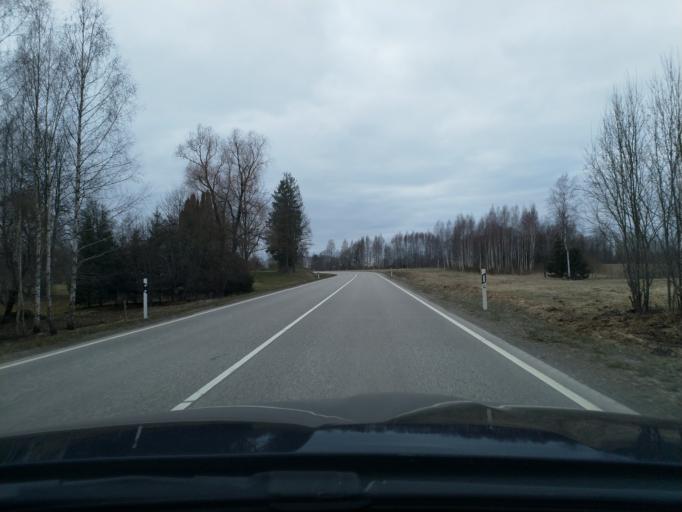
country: LV
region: Talsu Rajons
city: Sabile
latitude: 56.9485
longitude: 22.4763
